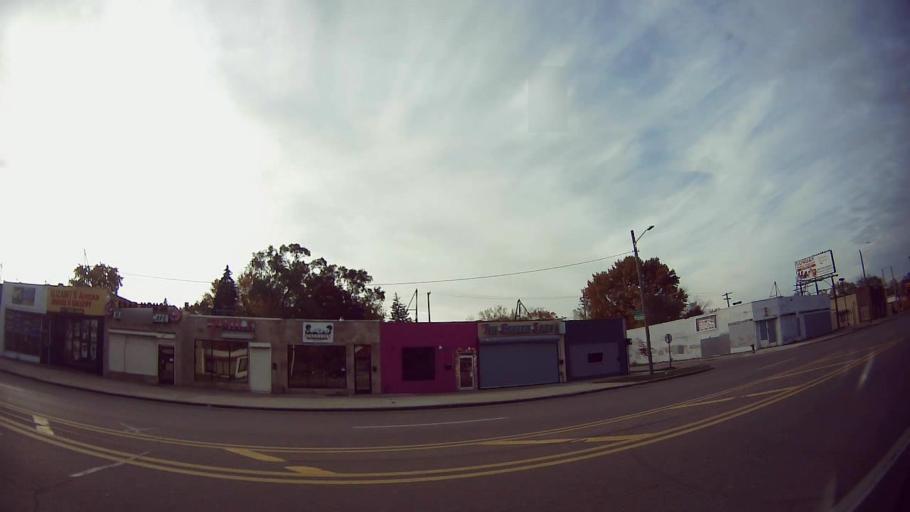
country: US
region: Michigan
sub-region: Oakland County
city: Southfield
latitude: 42.4297
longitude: -83.2374
